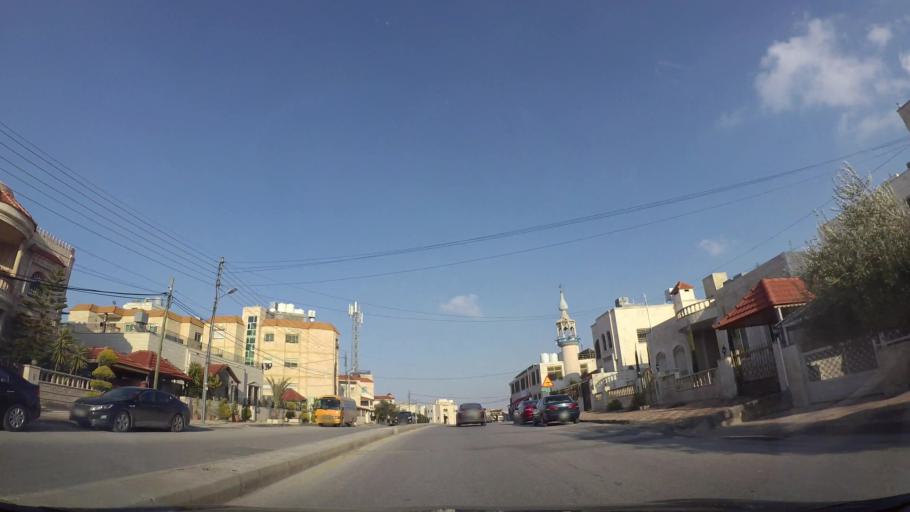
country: JO
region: Amman
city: Amman
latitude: 31.9854
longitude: 35.9466
